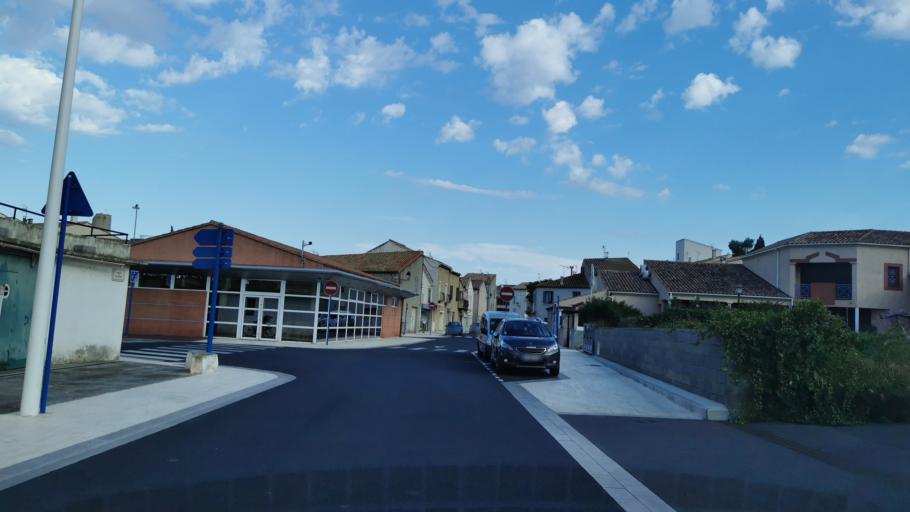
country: FR
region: Languedoc-Roussillon
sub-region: Departement de l'Aude
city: Gruissan
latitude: 43.1056
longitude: 3.0883
